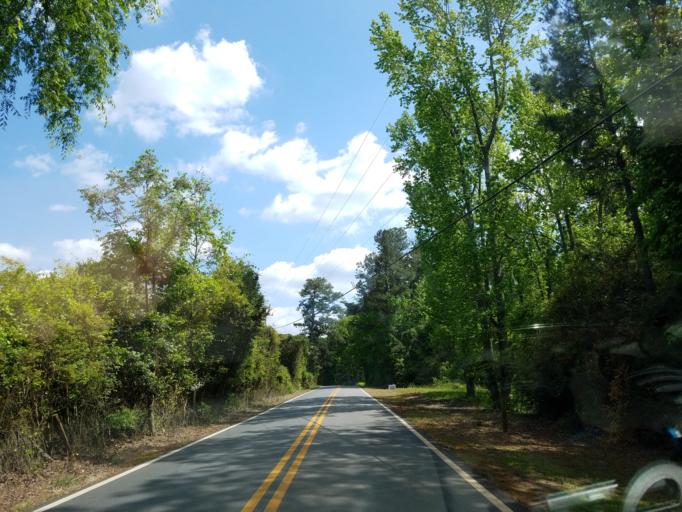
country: US
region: Georgia
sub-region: Monroe County
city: Forsyth
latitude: 33.0838
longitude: -83.9565
